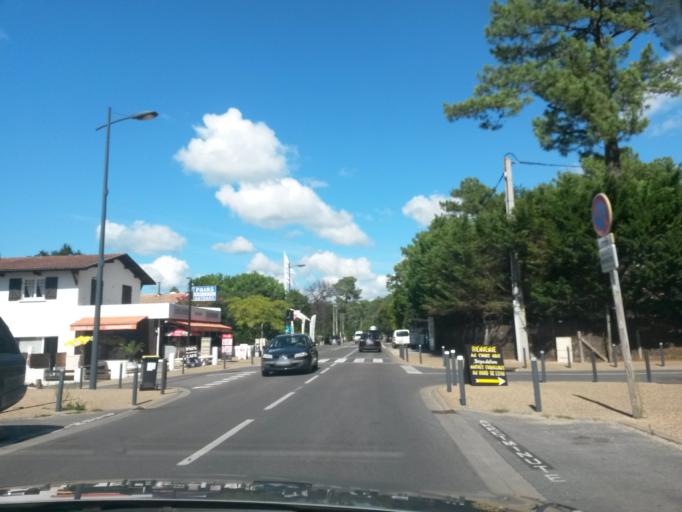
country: FR
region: Aquitaine
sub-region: Departement de la Gironde
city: Arcachon
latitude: 44.7165
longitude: -1.2126
